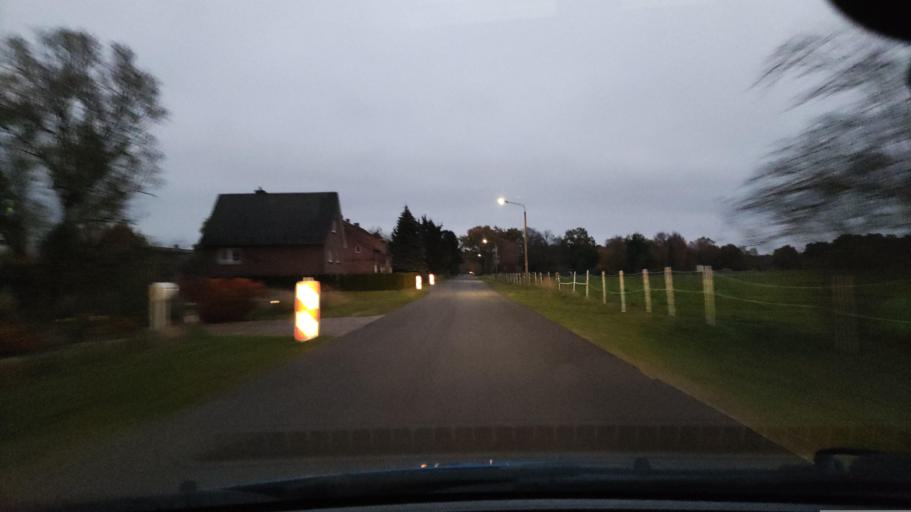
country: DE
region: Mecklenburg-Vorpommern
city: Domitz
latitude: 53.1679
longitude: 11.2225
